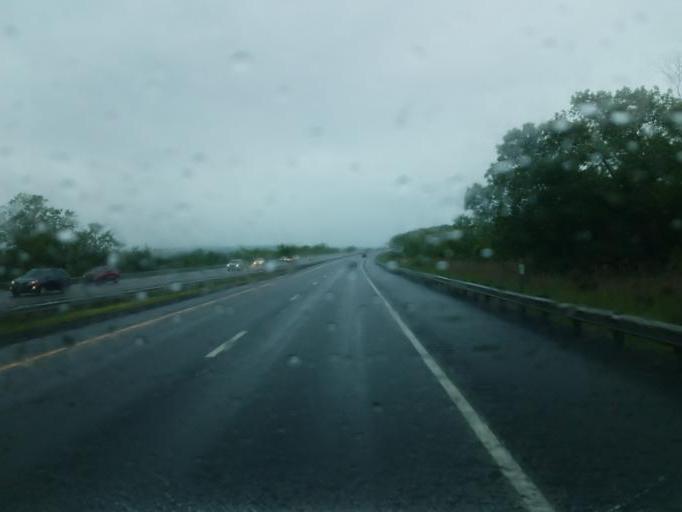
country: US
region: New York
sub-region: Herkimer County
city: Mohawk
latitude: 43.0174
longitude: -75.0021
